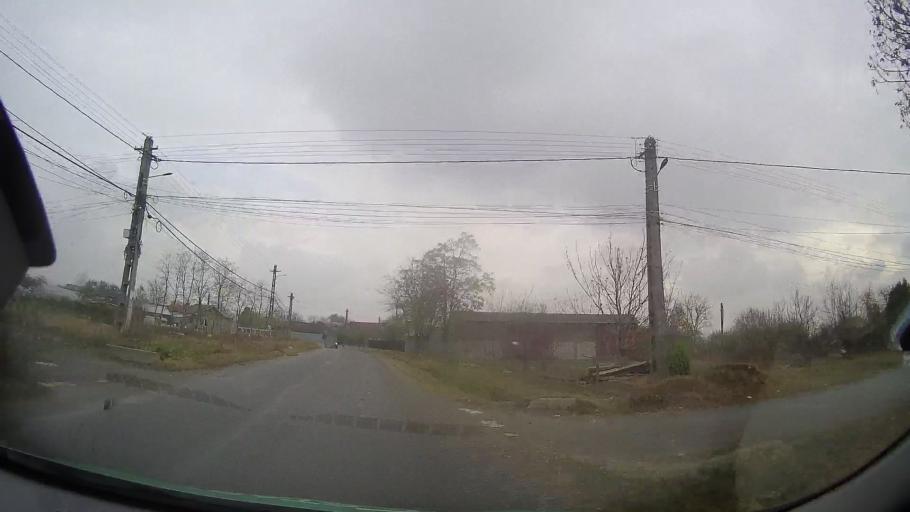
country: RO
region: Prahova
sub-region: Comuna Gherghita
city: Gherghita
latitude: 44.8008
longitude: 26.2750
